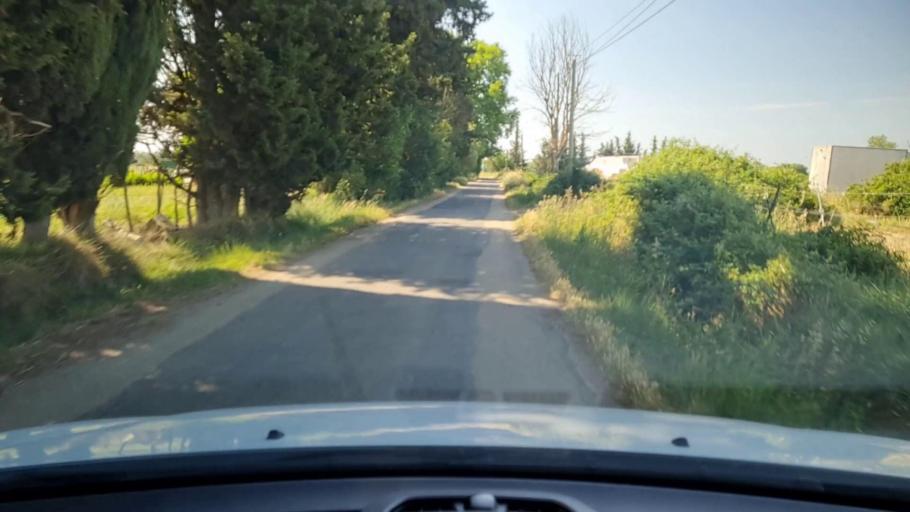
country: FR
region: Languedoc-Roussillon
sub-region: Departement du Gard
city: Le Cailar
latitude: 43.6551
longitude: 4.2371
